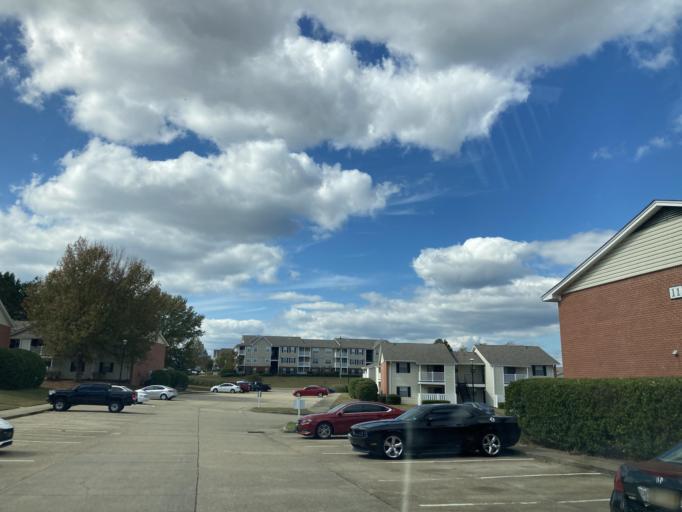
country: US
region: Mississippi
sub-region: Lamar County
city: Arnold Line
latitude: 31.3291
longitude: -89.3549
